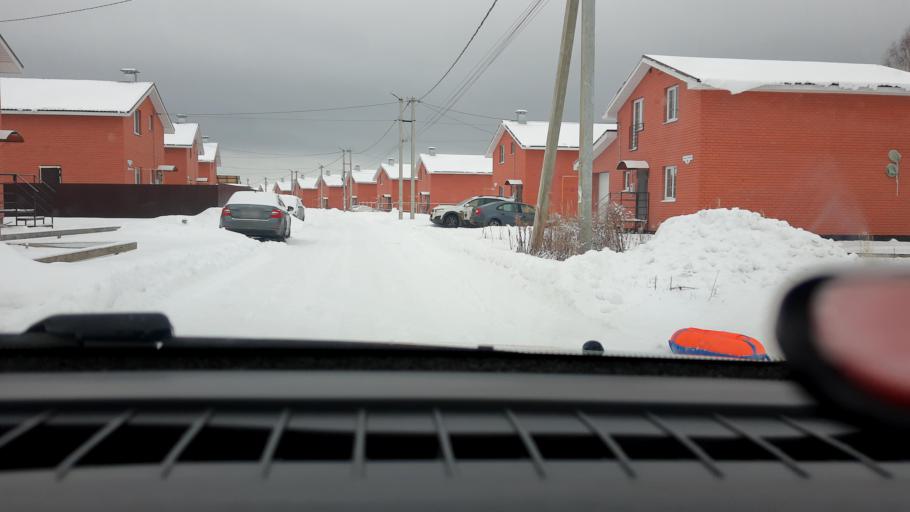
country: RU
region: Nizjnij Novgorod
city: Afonino
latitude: 56.1994
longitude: 44.0678
